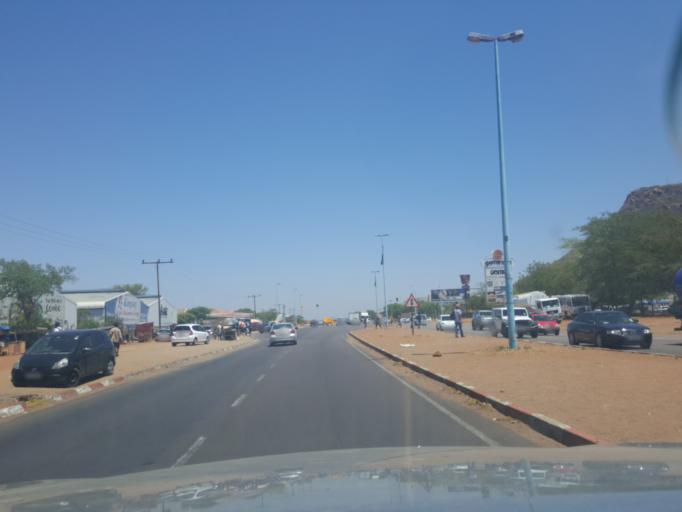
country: BW
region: South East
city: Gaborone
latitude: -24.6885
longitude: 25.8825
